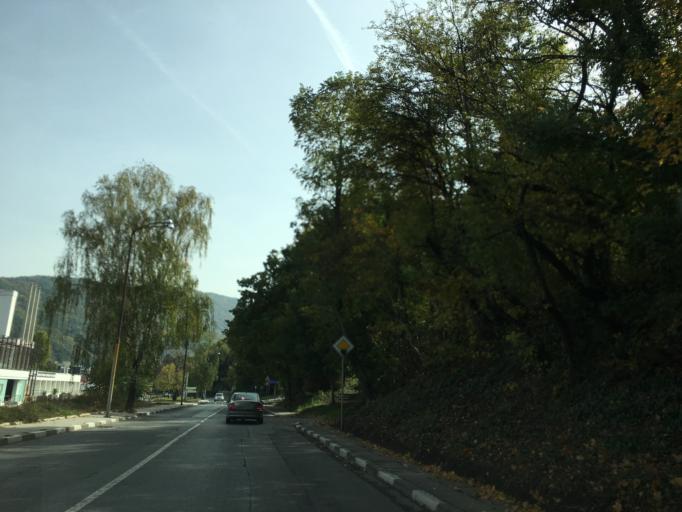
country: BG
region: Sofia-Capital
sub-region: Stolichna Obshtina
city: Sofia
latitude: 42.5971
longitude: 23.4079
